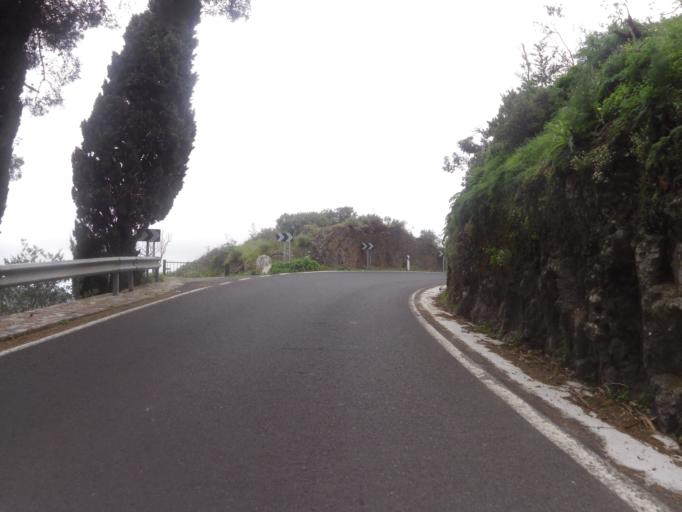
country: ES
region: Canary Islands
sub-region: Provincia de Las Palmas
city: Vega de San Mateo
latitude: 27.9997
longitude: -15.5343
